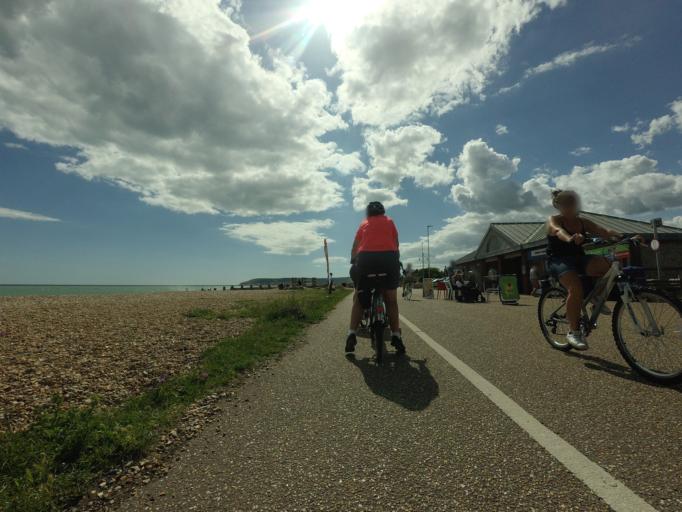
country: GB
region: England
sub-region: East Sussex
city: Pevensey
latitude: 50.7841
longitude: 0.3253
